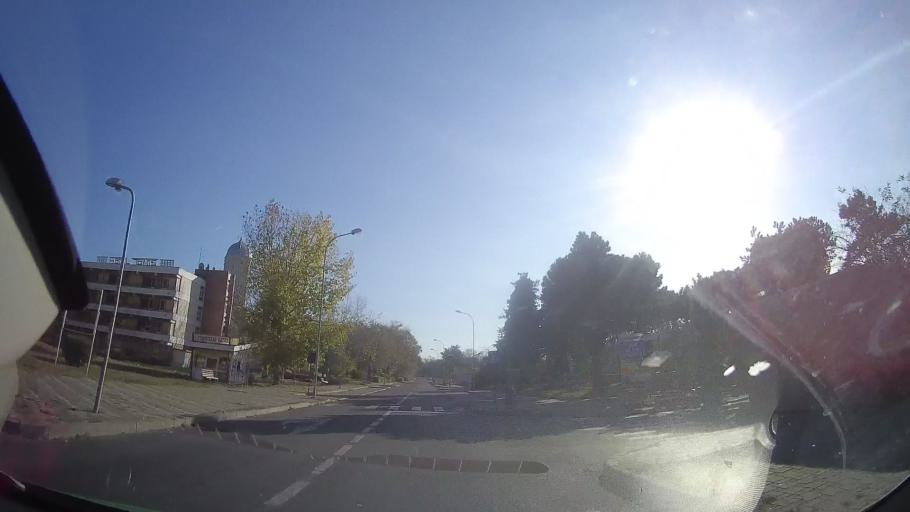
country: RO
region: Constanta
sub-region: Comuna Douazeci si Trei August
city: Douazeci si Trei August
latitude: 43.8643
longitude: 28.5977
